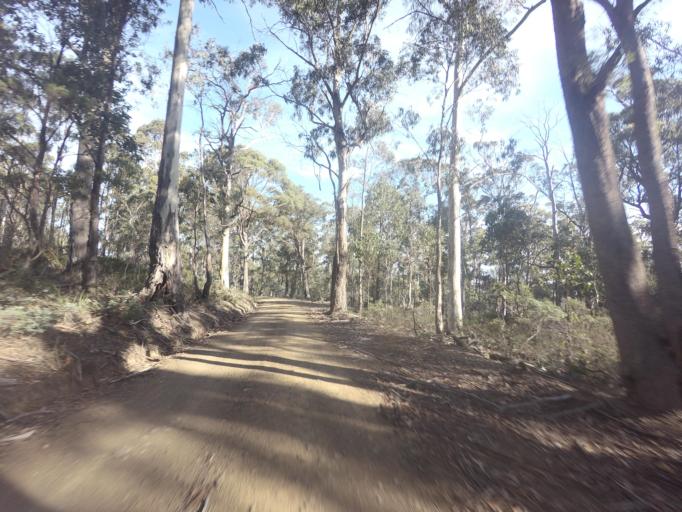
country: AU
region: Tasmania
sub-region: Sorell
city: Sorell
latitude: -42.5159
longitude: 147.4711
